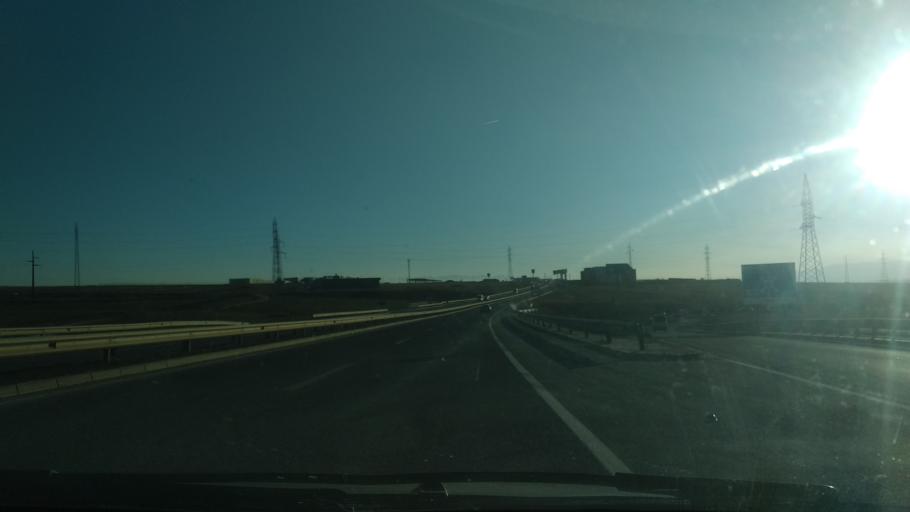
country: XK
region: Pristina
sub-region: Kosovo Polje
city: Kosovo Polje
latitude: 42.6850
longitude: 21.1181
